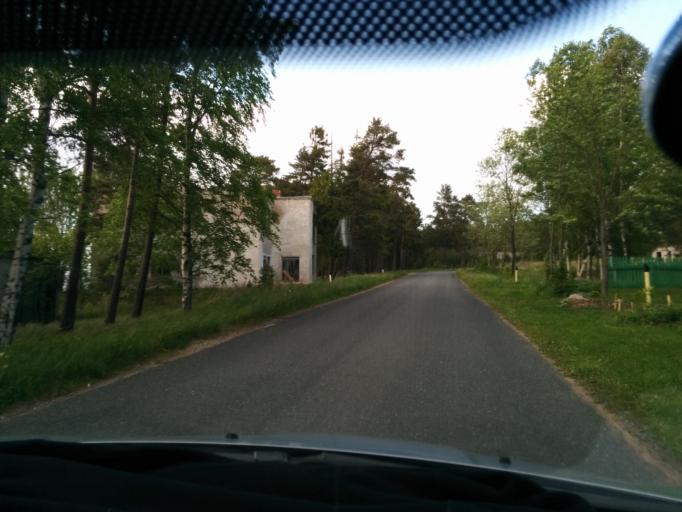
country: EE
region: Harju
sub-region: Loksa linn
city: Loksa
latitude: 59.6224
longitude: 25.6848
